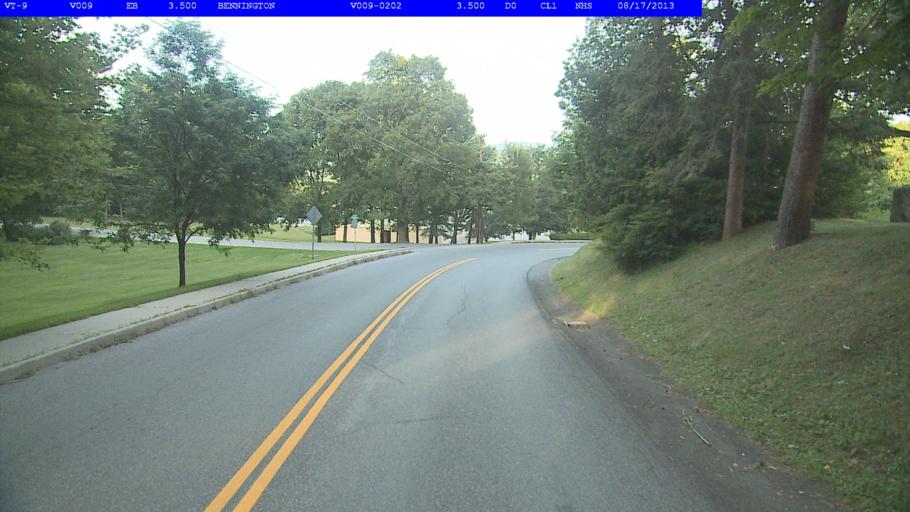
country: US
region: Vermont
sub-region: Bennington County
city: Bennington
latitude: 42.8845
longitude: -73.2124
